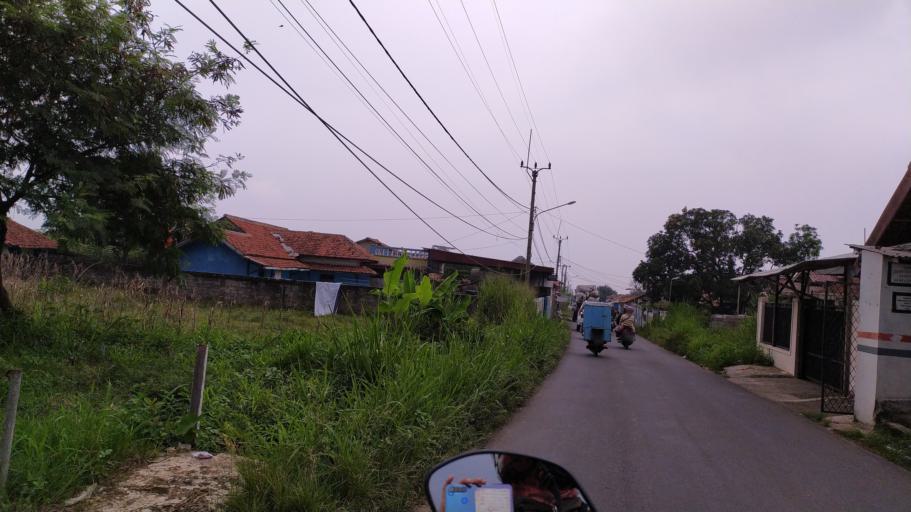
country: ID
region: West Java
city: Ciampea
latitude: -6.6000
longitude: 106.7033
